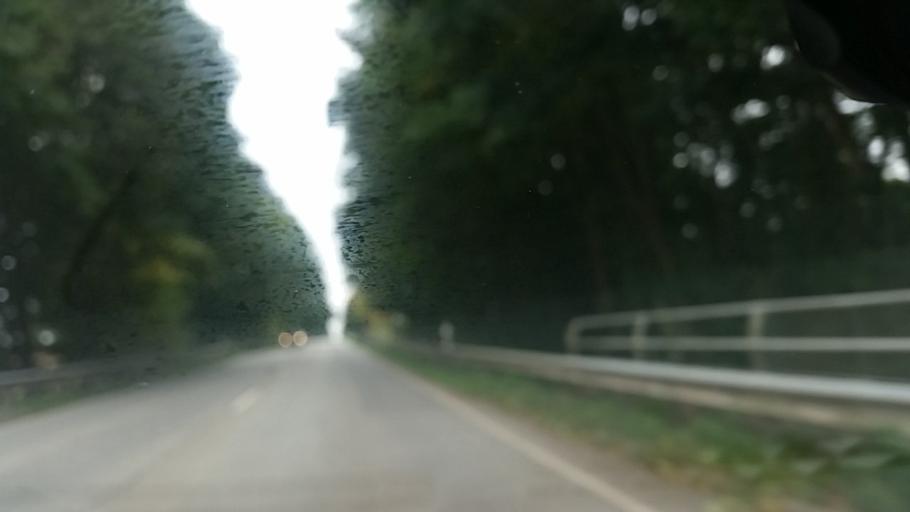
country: DE
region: Schleswig-Holstein
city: Mozen
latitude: 53.9074
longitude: 10.2619
